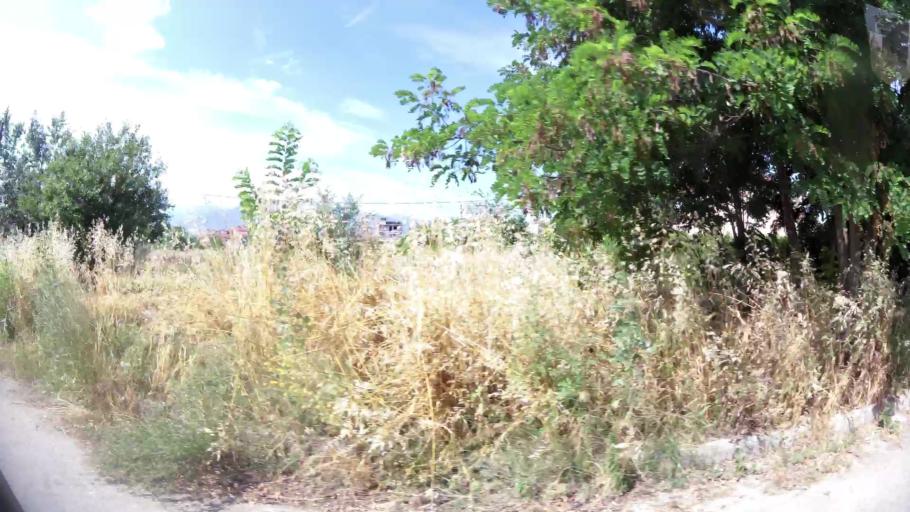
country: GR
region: Central Macedonia
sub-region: Nomos Pierias
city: Katerini
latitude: 40.2785
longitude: 22.4904
